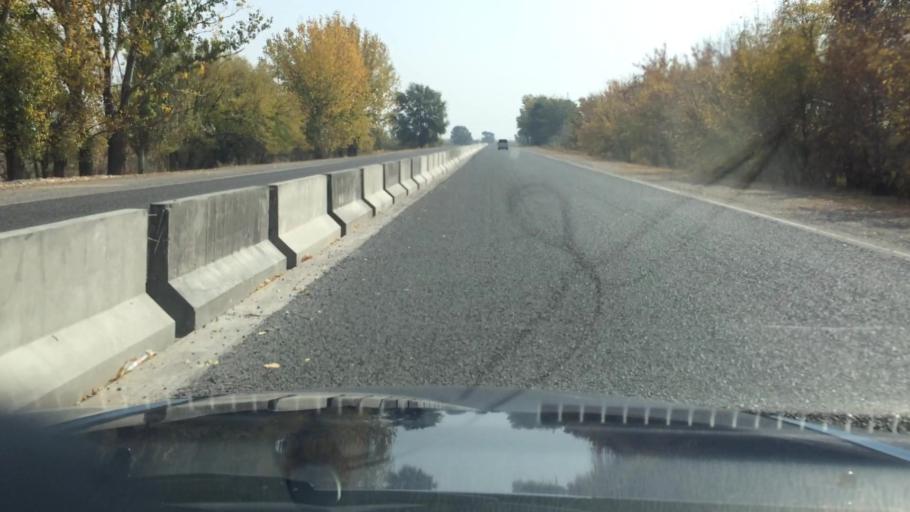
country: KG
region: Chuy
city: Kant
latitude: 42.9631
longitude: 74.9168
